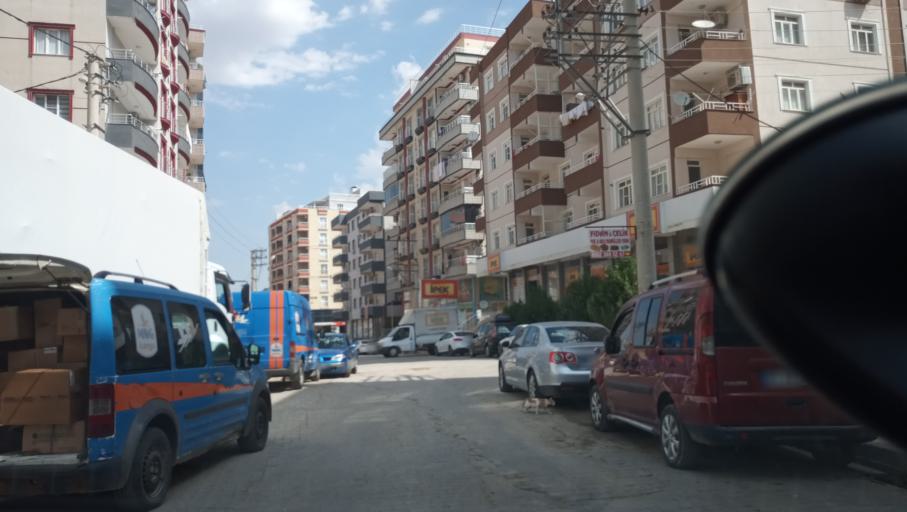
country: TR
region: Mardin
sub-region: Mardin Ilcesi
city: Mardin
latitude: 37.3275
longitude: 40.7176
